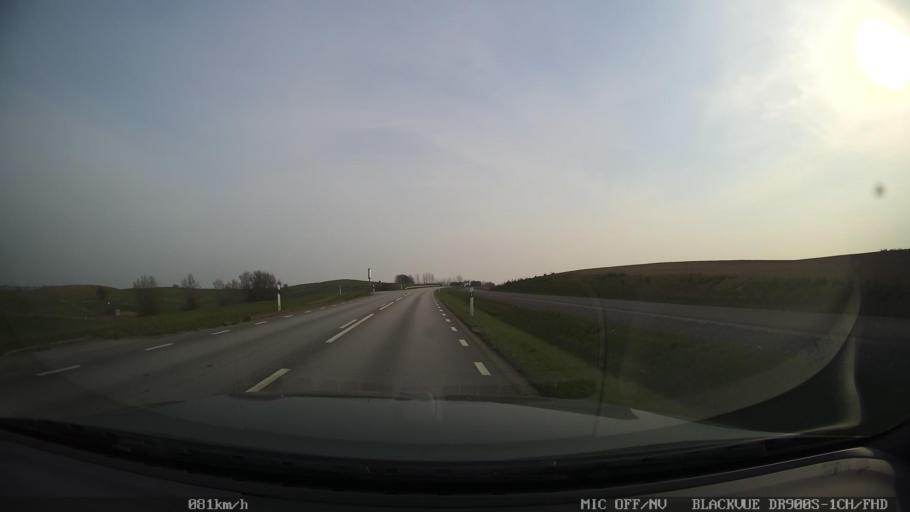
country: SE
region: Skane
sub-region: Ystads Kommun
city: Ystad
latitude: 55.4651
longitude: 13.7989
